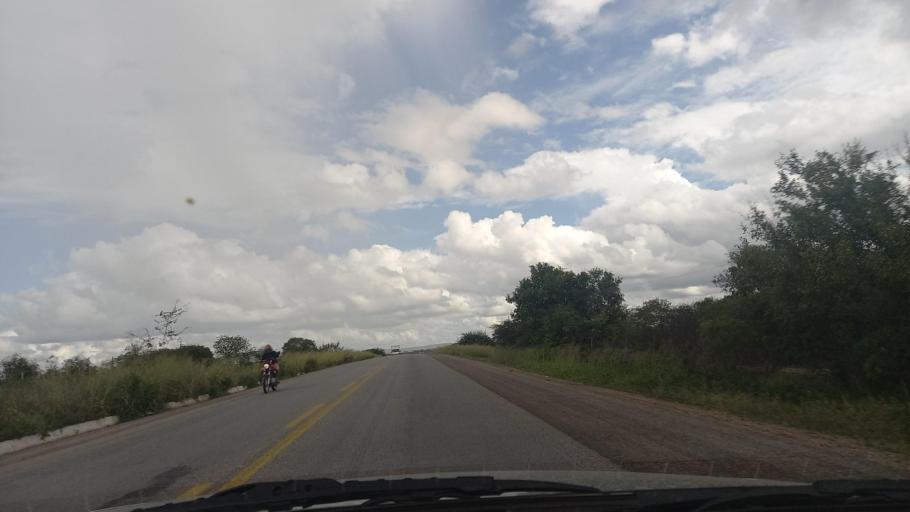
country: BR
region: Pernambuco
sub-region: Cachoeirinha
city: Cachoeirinha
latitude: -8.5448
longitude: -36.2702
